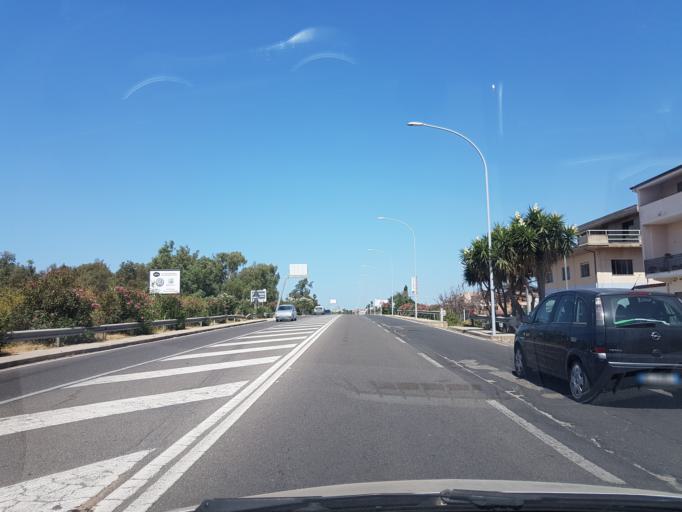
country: IT
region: Sardinia
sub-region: Provincia di Oristano
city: Santa Giusta
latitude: 39.8878
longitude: 8.6020
